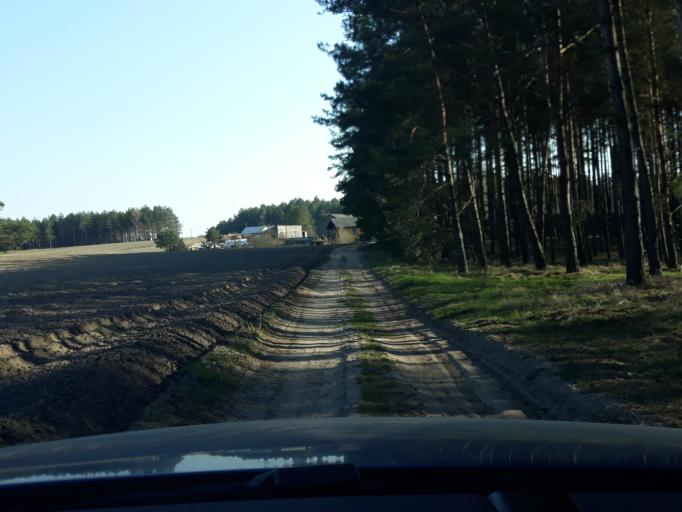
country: PL
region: Pomeranian Voivodeship
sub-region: Powiat bytowski
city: Lipnica
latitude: 53.8940
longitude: 17.4944
